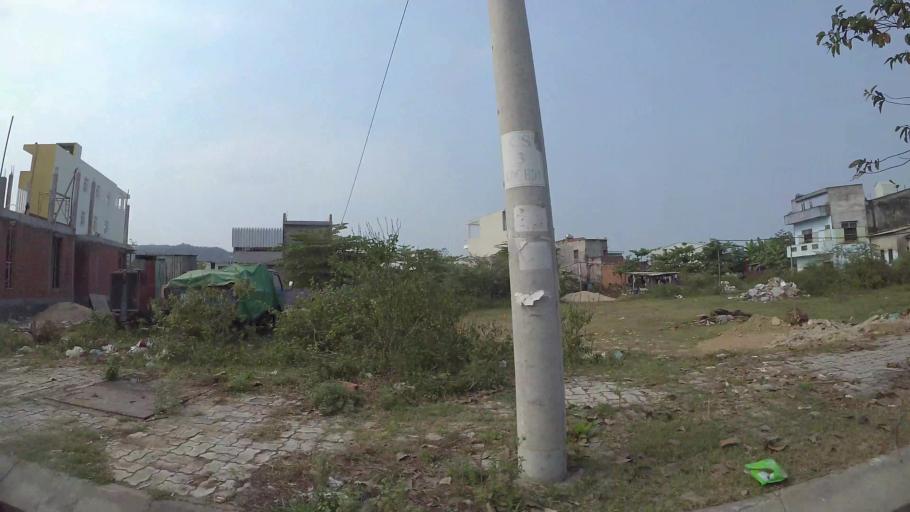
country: VN
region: Da Nang
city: Lien Chieu
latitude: 16.0502
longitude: 108.1505
